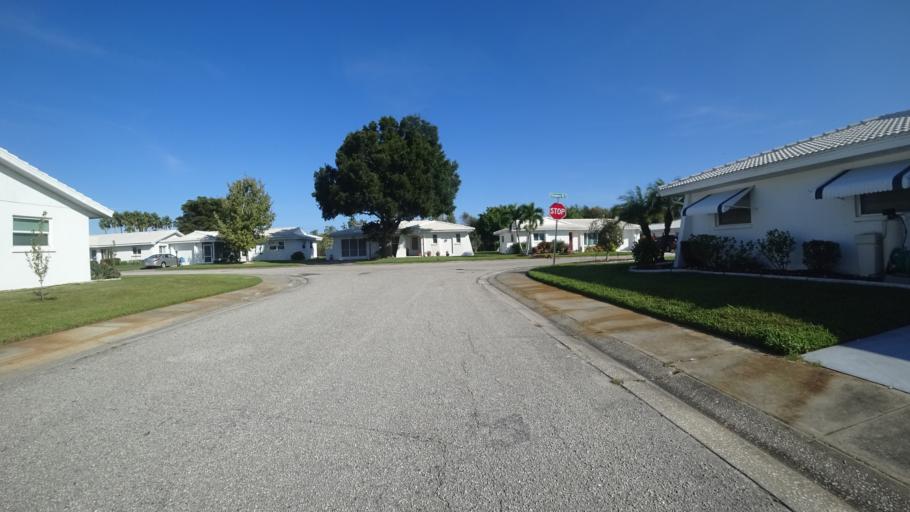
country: US
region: Florida
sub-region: Manatee County
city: Ellenton
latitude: 27.4968
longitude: -82.5116
